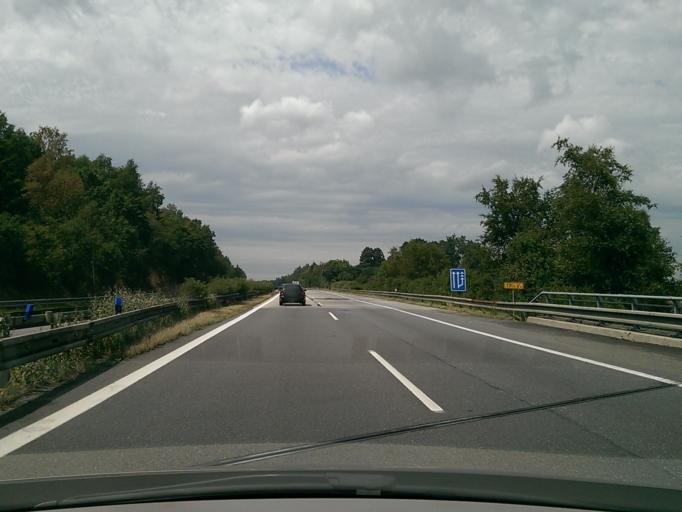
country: CZ
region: Vysocina
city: Merin
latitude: 49.4033
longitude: 15.8456
